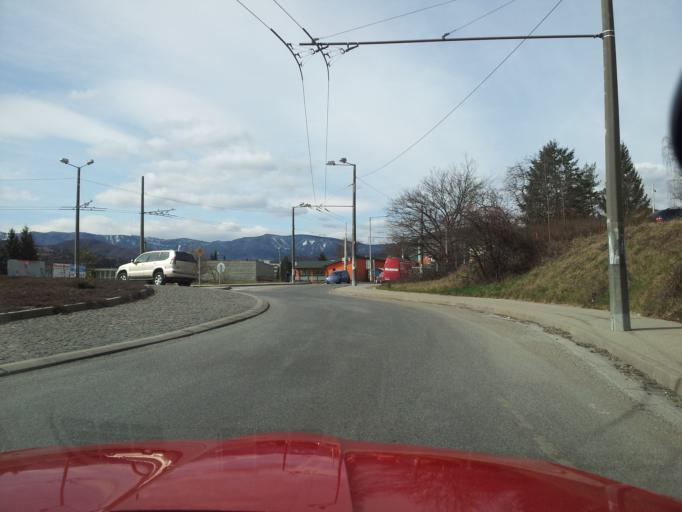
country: SK
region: Banskobystricky
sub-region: Okres Banska Bystrica
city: Banska Bystrica
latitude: 48.7395
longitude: 19.1283
